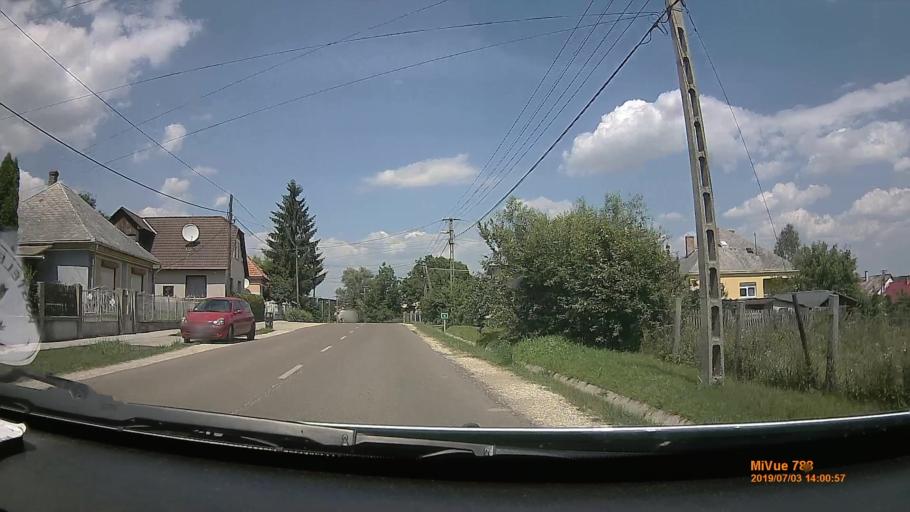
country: HU
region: Borsod-Abauj-Zemplen
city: Kazincbarcika
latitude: 48.1815
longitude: 20.6523
